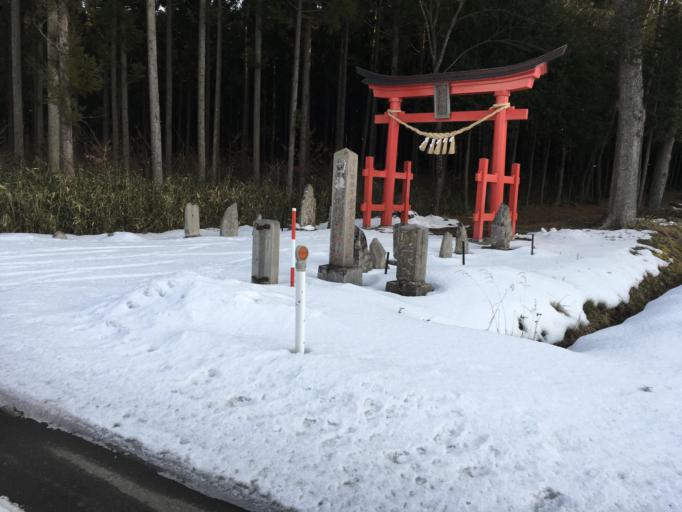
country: JP
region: Iwate
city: Ichinoseki
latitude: 38.8161
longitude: 141.0065
